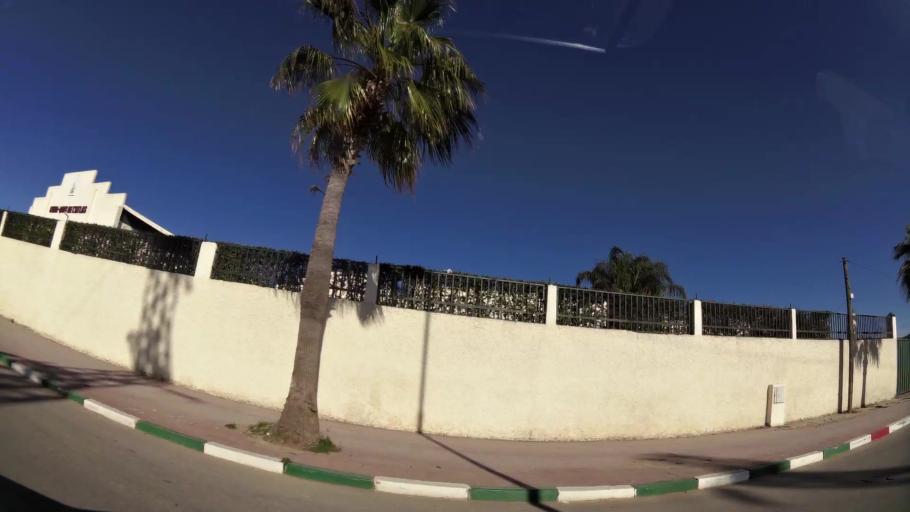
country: MA
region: Meknes-Tafilalet
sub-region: Meknes
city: Meknes
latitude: 33.8744
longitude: -5.5747
